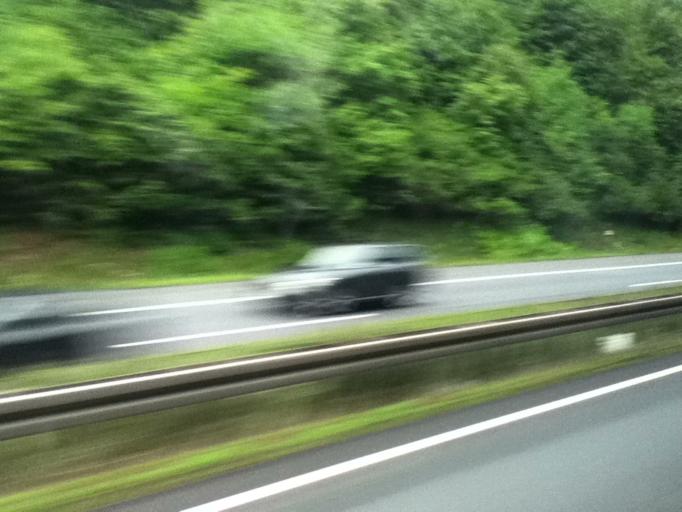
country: DE
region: Hesse
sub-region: Regierungsbezirk Giessen
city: Giessen
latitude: 50.5585
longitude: 8.6631
